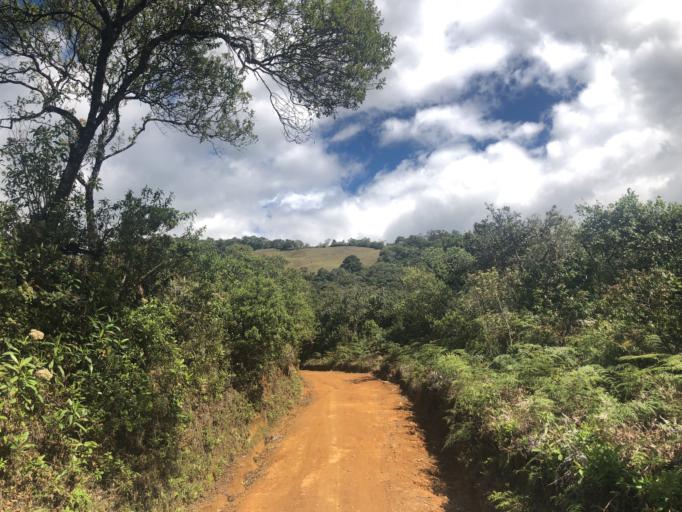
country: CO
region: Cauca
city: Silvia
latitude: 2.6792
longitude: -76.4394
